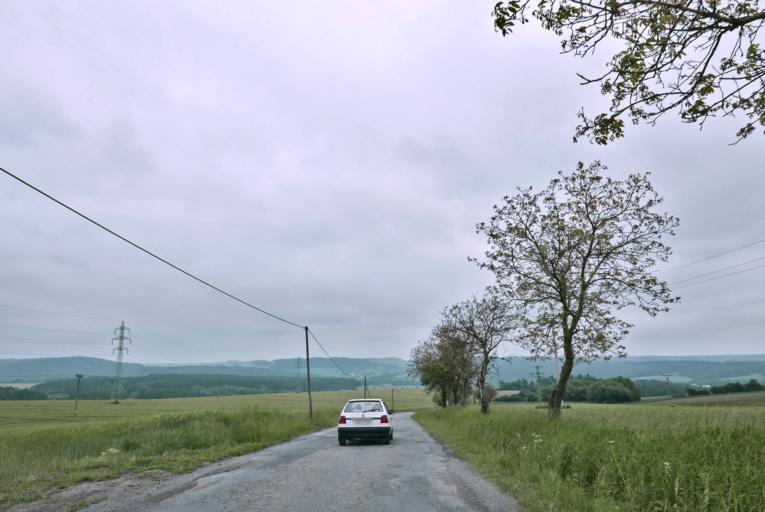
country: CZ
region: Plzensky
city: Zihle
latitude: 49.9931
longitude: 13.3404
